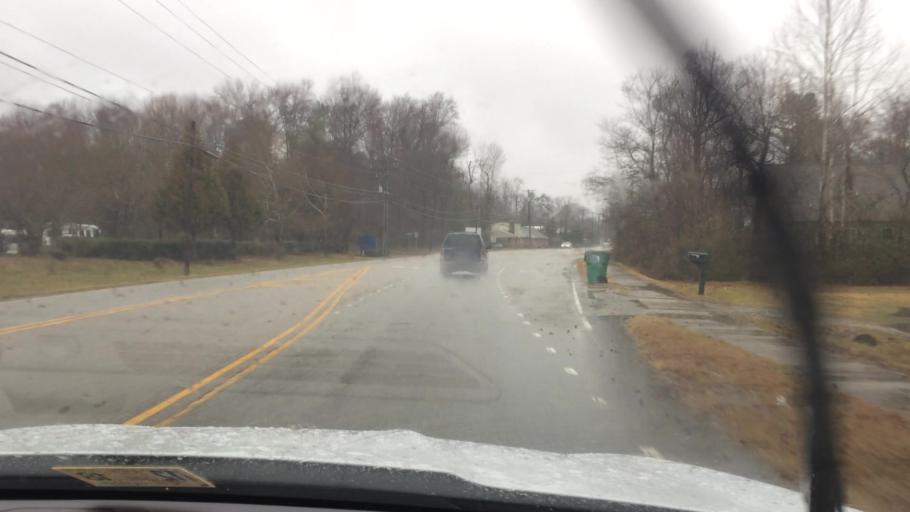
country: US
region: Virginia
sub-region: City of Williamsburg
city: Williamsburg
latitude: 37.2201
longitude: -76.6254
